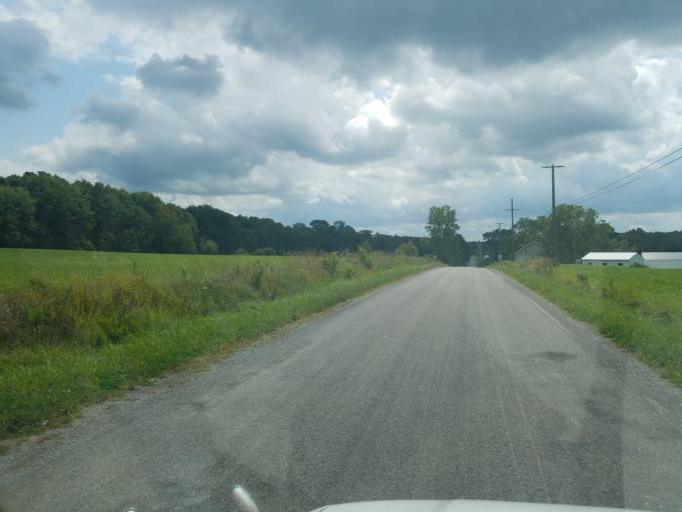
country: US
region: Ohio
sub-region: Geauga County
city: Middlefield
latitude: 41.5155
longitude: -81.0855
